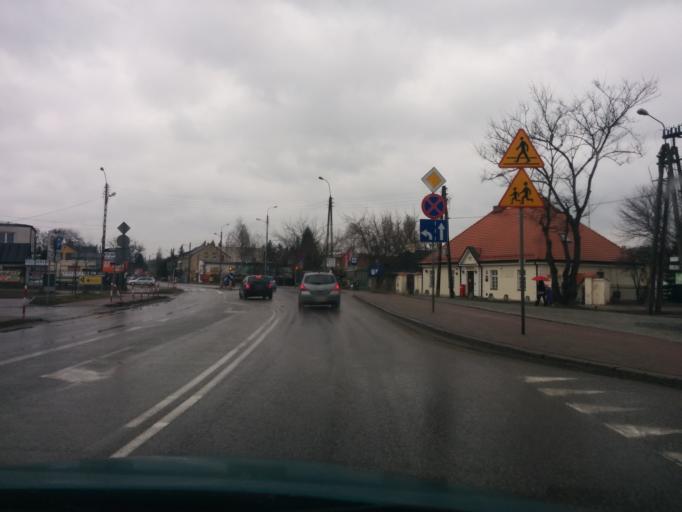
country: PL
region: Masovian Voivodeship
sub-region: Powiat legionowski
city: Jablonna
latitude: 52.3752
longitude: 20.9249
